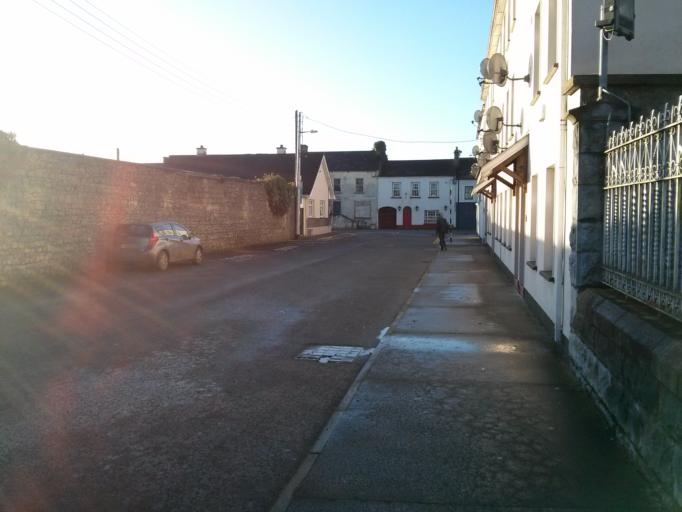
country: IE
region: Leinster
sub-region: Uibh Fhaili
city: Tullamore
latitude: 53.2765
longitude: -7.4894
